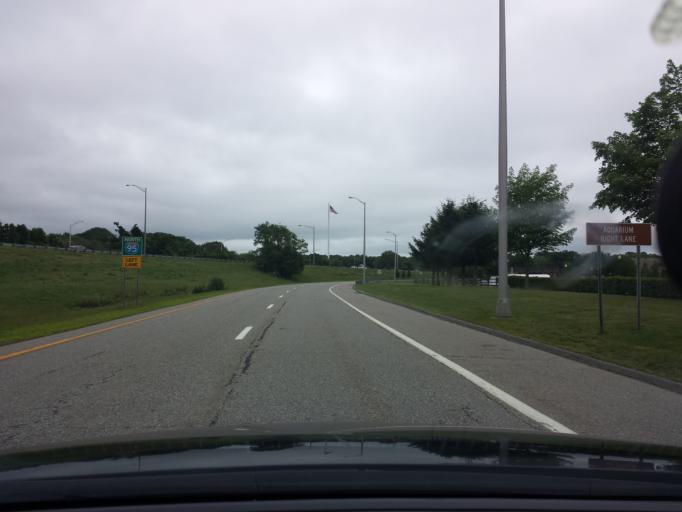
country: US
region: Connecticut
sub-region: New London County
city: Old Mystic
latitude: 41.3745
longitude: -71.9579
